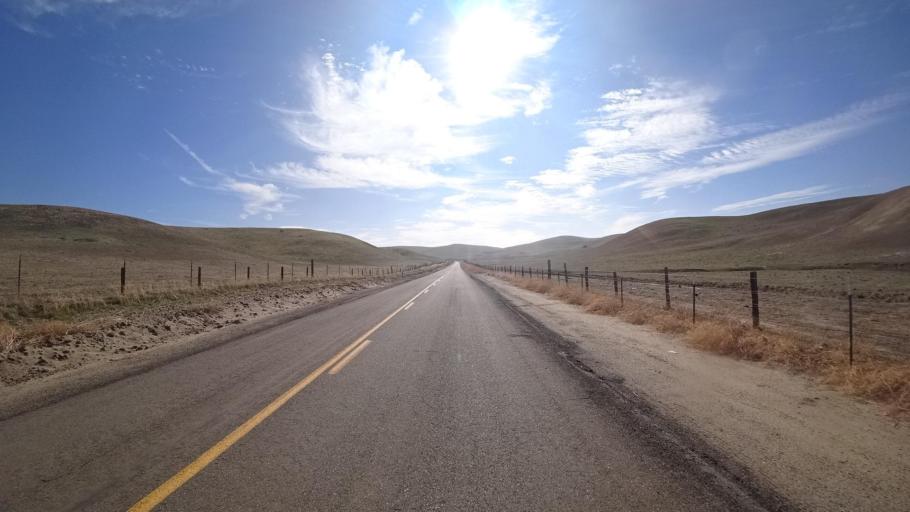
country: US
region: California
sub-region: Kern County
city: Oildale
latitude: 35.6360
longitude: -118.9439
